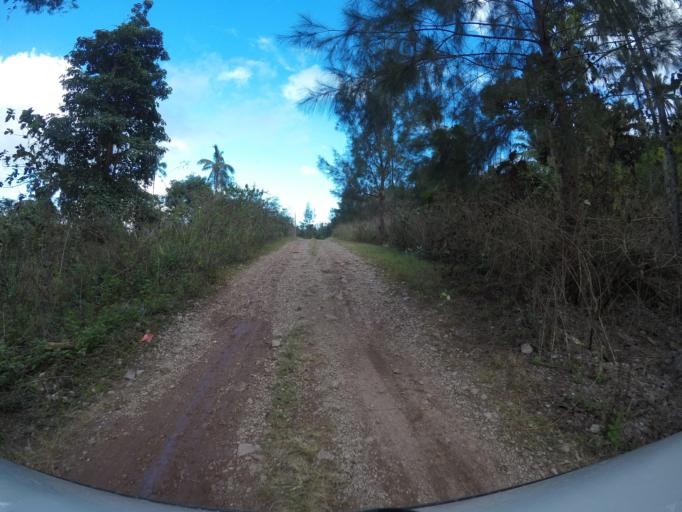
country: TL
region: Baucau
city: Venilale
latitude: -8.6828
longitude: 126.6516
